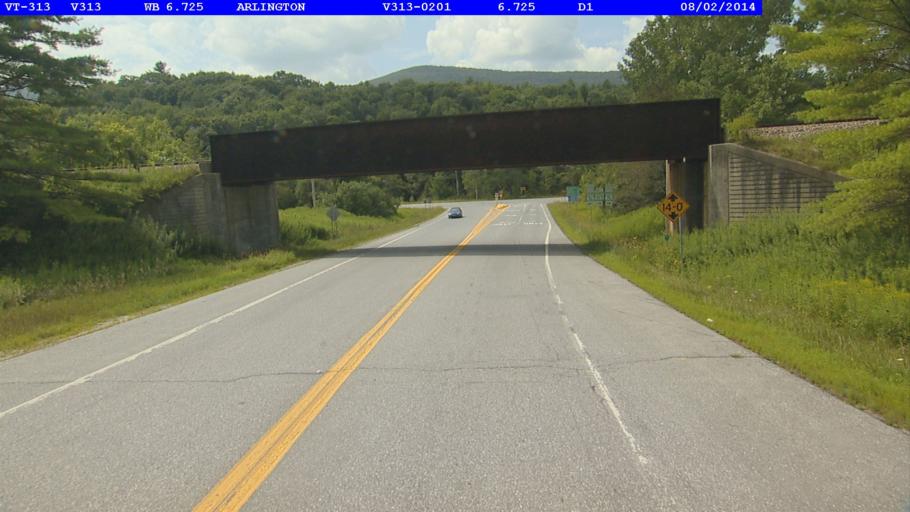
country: US
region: Vermont
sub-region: Bennington County
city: Arlington
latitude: 43.0552
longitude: -73.1614
